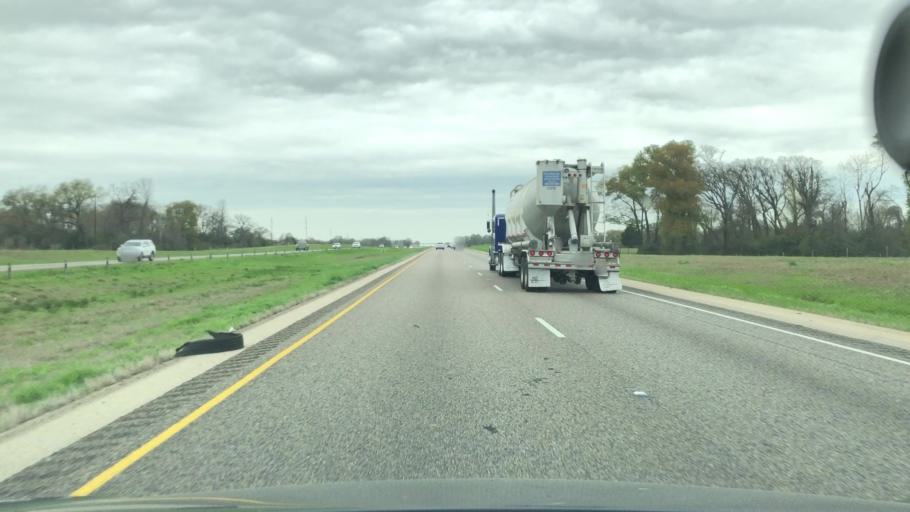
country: US
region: Texas
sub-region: Madison County
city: Madisonville
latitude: 31.0544
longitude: -95.9480
